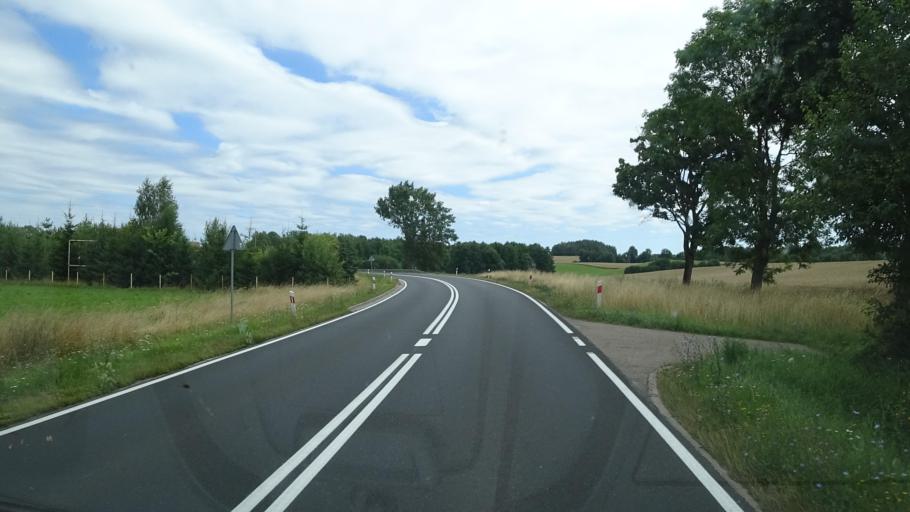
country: PL
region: Warmian-Masurian Voivodeship
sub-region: Powiat elcki
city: Elk
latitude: 53.7983
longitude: 22.2395
